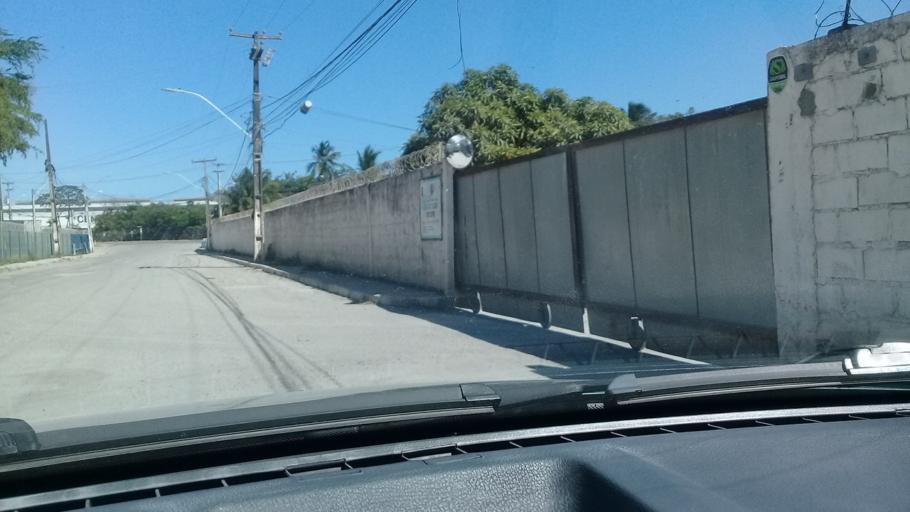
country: BR
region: Pernambuco
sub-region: Jaboatao Dos Guararapes
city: Jaboatao
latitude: -8.1542
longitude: -34.9492
